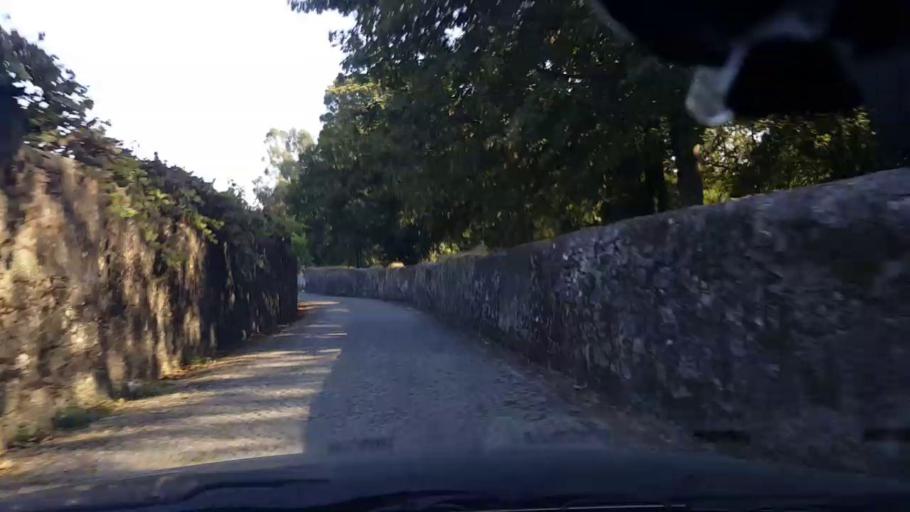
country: PT
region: Porto
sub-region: Vila do Conde
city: Arvore
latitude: 41.3414
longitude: -8.6862
